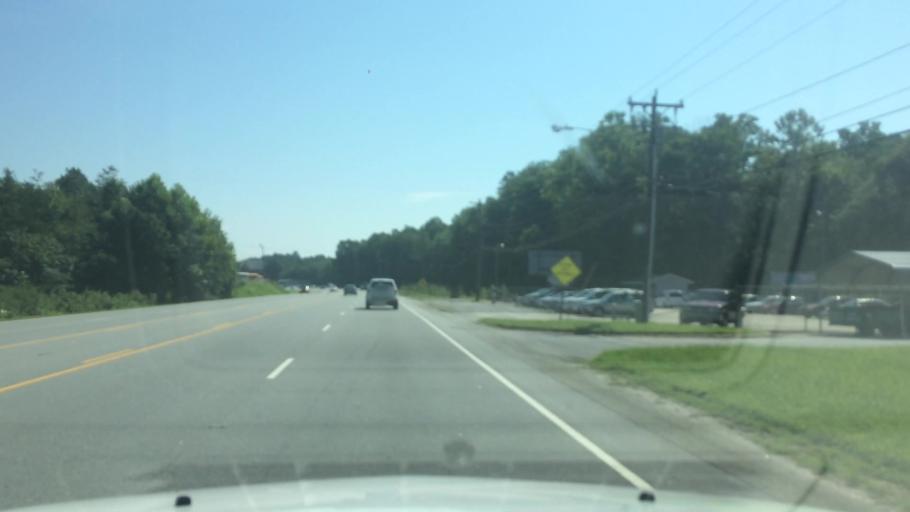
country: US
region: North Carolina
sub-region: Caldwell County
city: Lenoir
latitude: 35.9186
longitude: -81.5118
